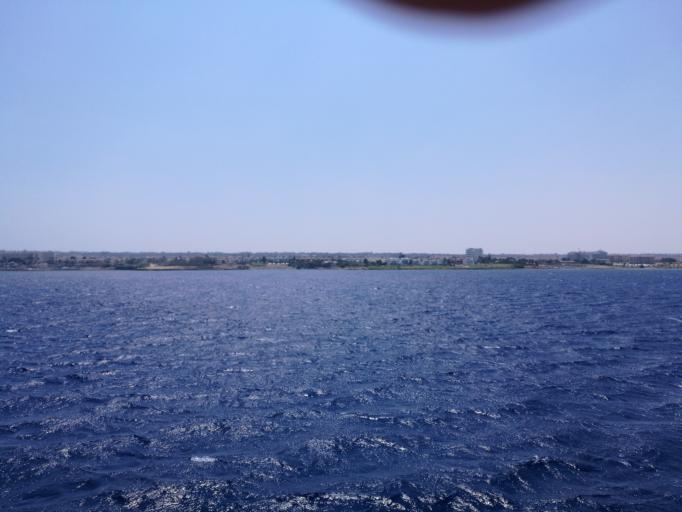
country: CY
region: Ammochostos
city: Protaras
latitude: 35.0462
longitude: 34.0414
